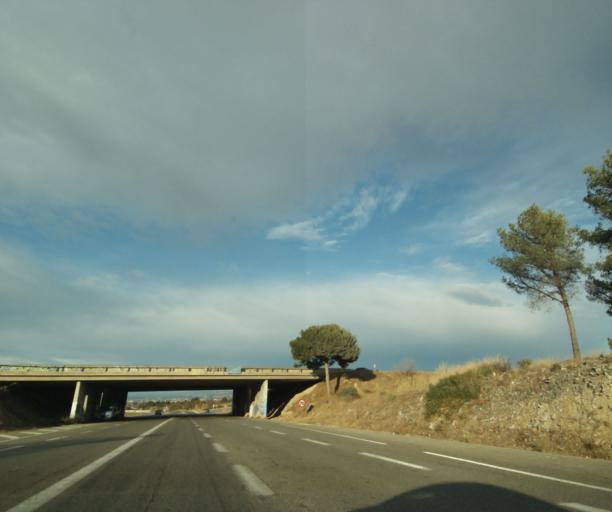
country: FR
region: Provence-Alpes-Cote d'Azur
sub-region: Departement des Bouches-du-Rhone
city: Chateauneuf-les-Martigues
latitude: 43.3725
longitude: 5.1851
